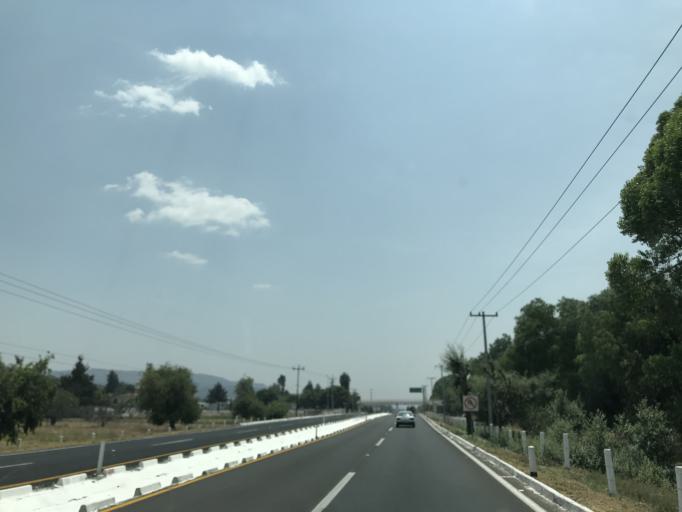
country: MX
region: Tlaxcala
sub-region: Ixtacuixtla de Mariano Matamoros
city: Santa Justina Ecatepec
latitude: 19.3274
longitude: -98.3372
